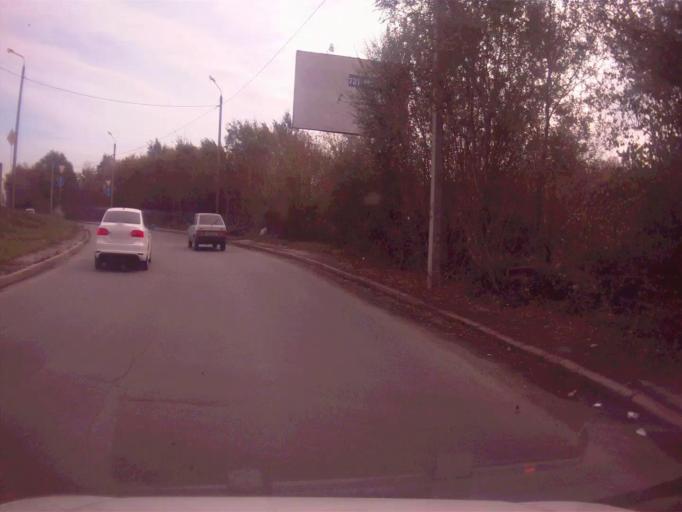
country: RU
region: Chelyabinsk
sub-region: Gorod Chelyabinsk
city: Chelyabinsk
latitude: 55.1600
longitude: 61.4288
